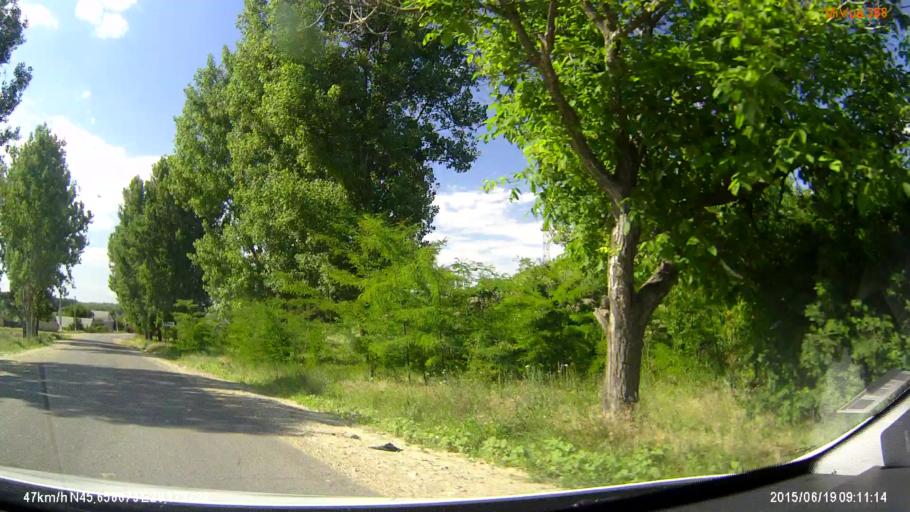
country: RO
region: Galati
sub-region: Comuna Frumusita
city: Frumusita
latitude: 45.6585
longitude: 28.1737
